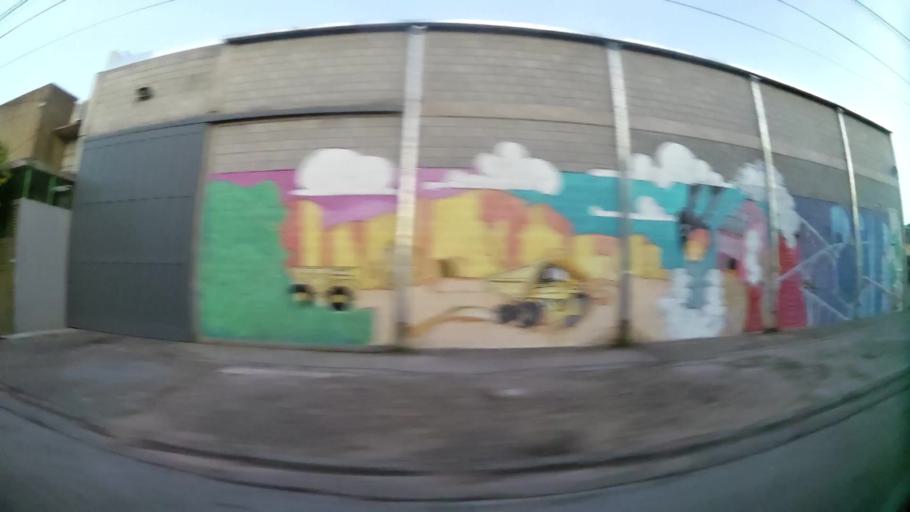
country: AR
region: Buenos Aires
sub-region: Partido de Moron
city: Moron
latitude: -34.6592
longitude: -58.6331
